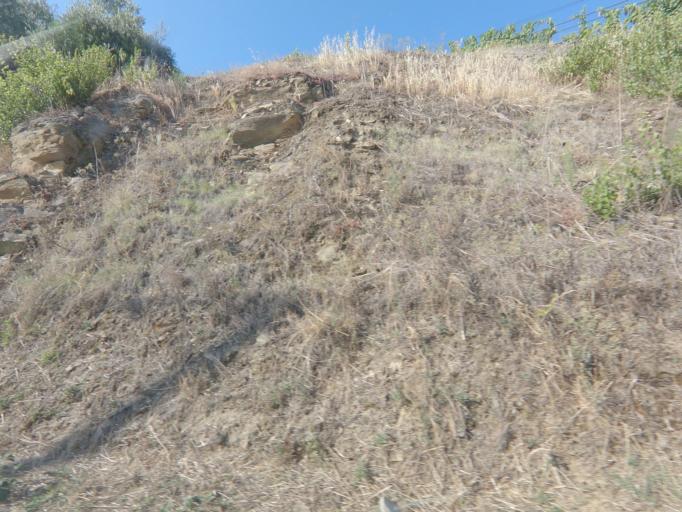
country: PT
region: Vila Real
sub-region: Sabrosa
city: Vilela
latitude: 41.1761
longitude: -7.5786
